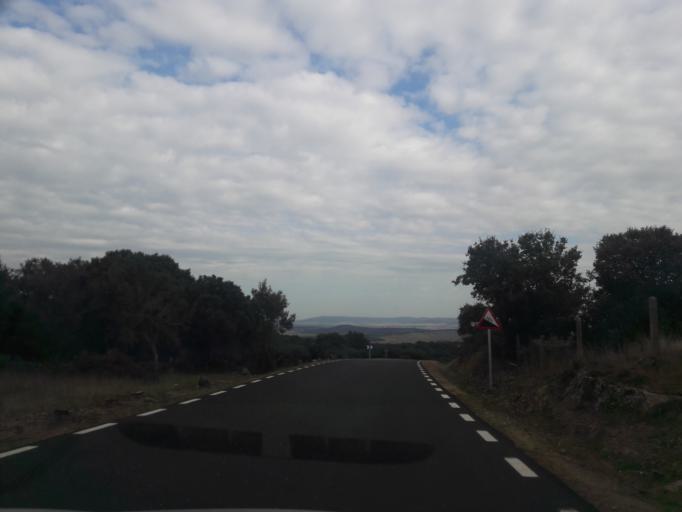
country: ES
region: Castille and Leon
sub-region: Provincia de Salamanca
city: Pastores
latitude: 40.5114
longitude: -6.5287
